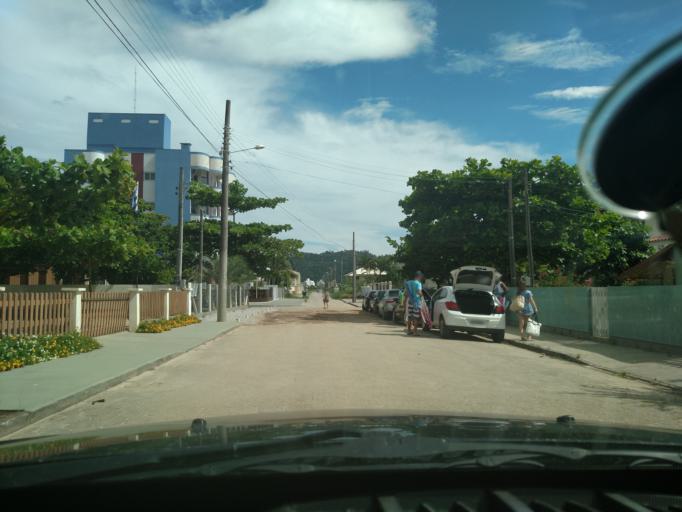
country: BR
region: Santa Catarina
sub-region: Tijucas
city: Tijucas
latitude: -27.3314
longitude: -48.5355
